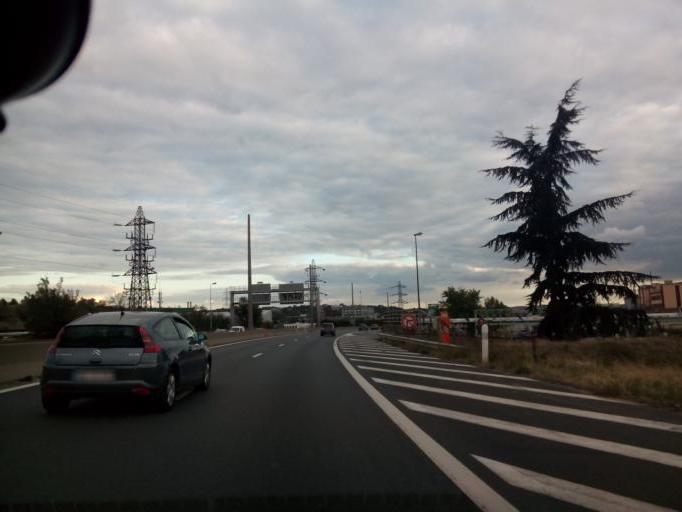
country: FR
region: Rhone-Alpes
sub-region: Departement du Rhone
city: Pierre-Benite
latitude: 45.6928
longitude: 4.8445
